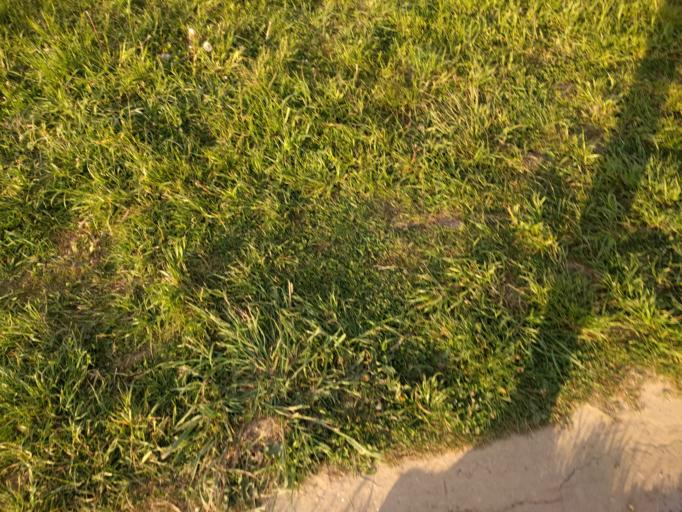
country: BE
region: Flanders
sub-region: Provincie West-Vlaanderen
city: Kortrijk
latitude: 50.8006
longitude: 3.2293
